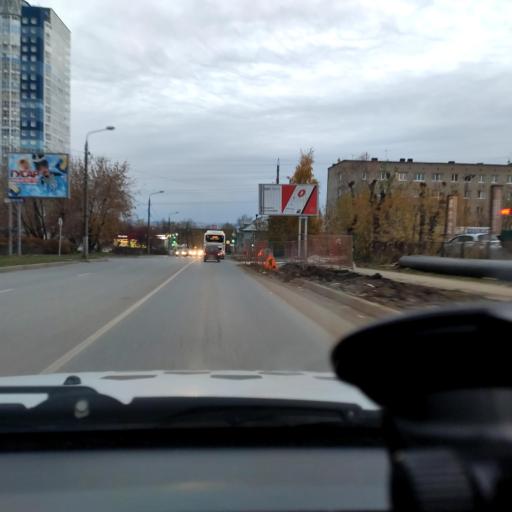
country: RU
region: Perm
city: Kondratovo
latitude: 57.9694
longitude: 56.1728
